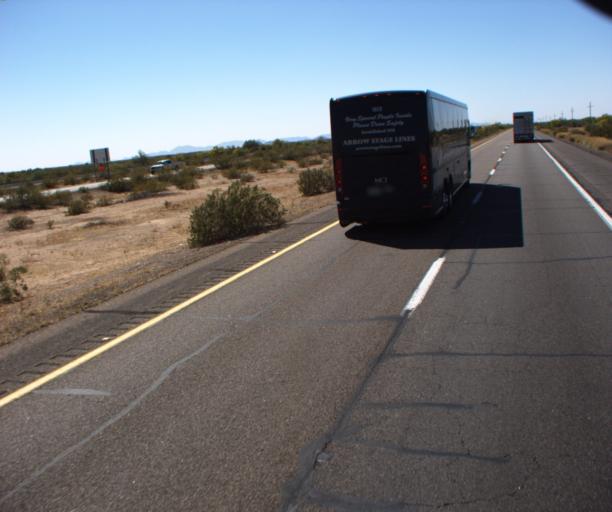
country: US
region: Arizona
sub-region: Maricopa County
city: Gila Bend
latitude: 32.8451
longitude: -113.2856
